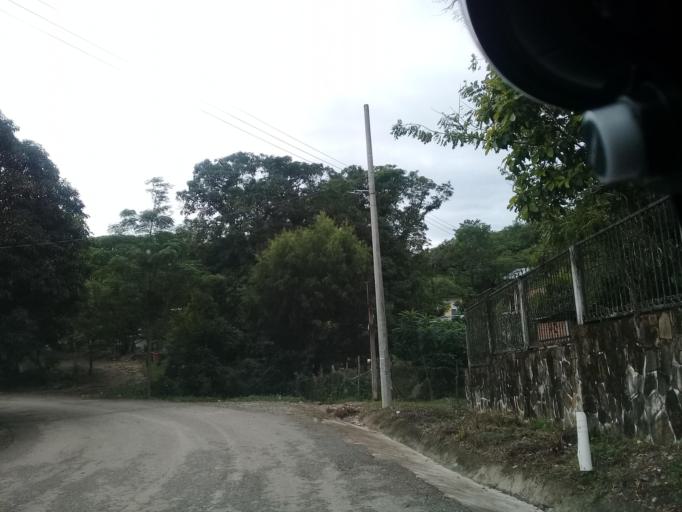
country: MX
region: Hidalgo
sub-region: Huejutla de Reyes
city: Chalahuiyapa
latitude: 21.1959
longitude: -98.3327
